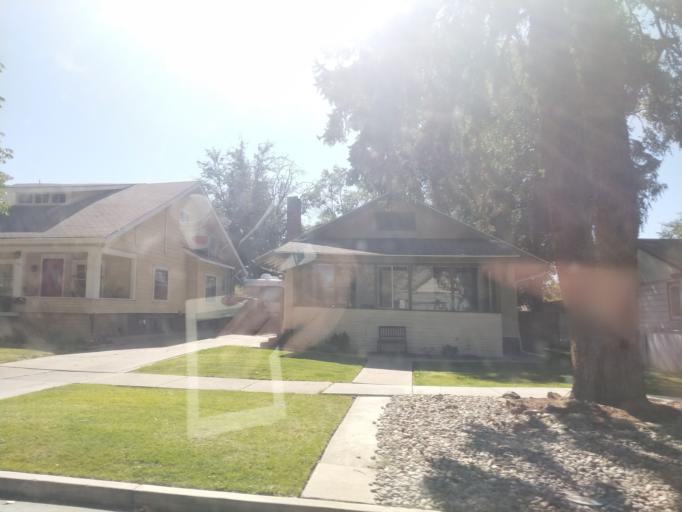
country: US
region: Colorado
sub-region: Mesa County
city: Grand Junction
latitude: 39.0723
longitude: -108.5535
